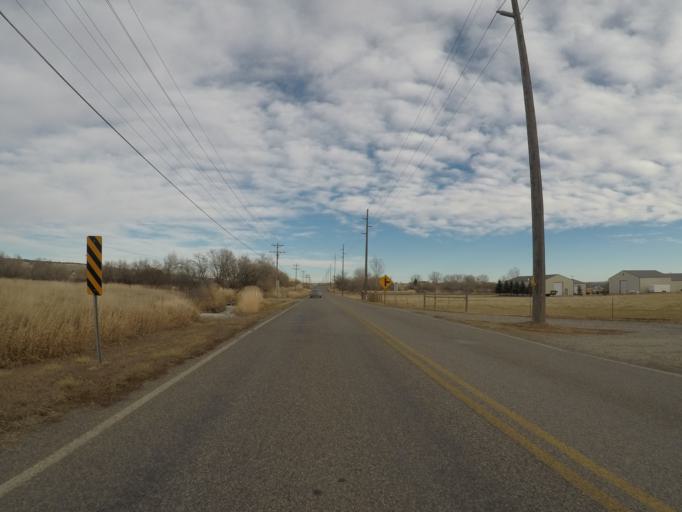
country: US
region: Montana
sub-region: Yellowstone County
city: Laurel
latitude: 45.7841
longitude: -108.6823
